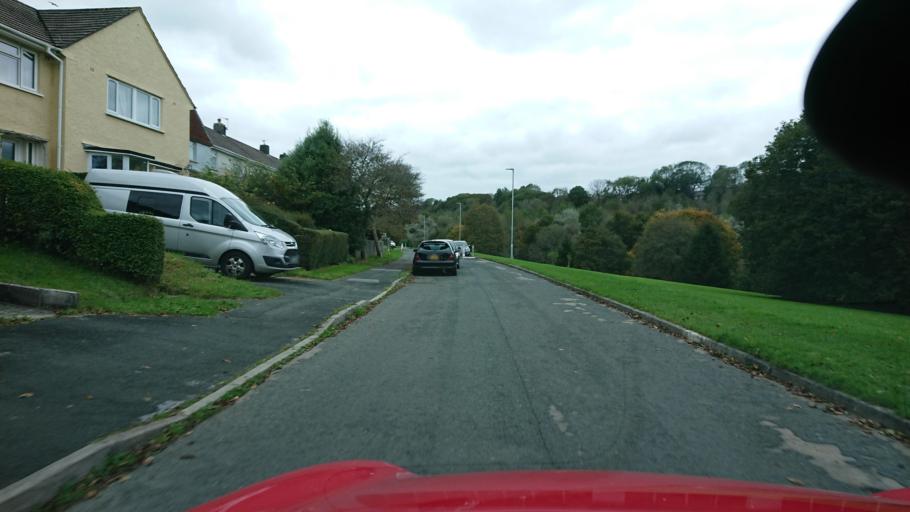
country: GB
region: England
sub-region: Plymouth
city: Plymouth
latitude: 50.4154
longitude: -4.1497
